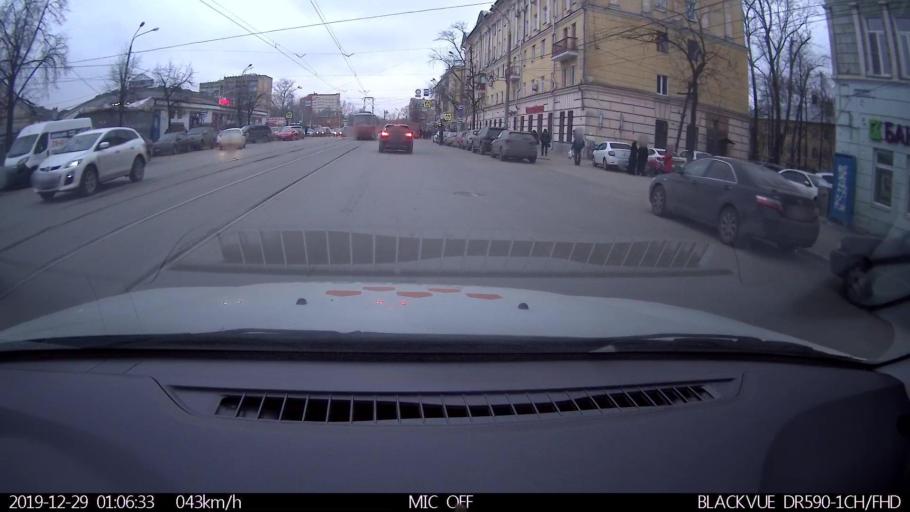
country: RU
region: Nizjnij Novgorod
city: Nizhniy Novgorod
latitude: 56.3175
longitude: 43.9423
